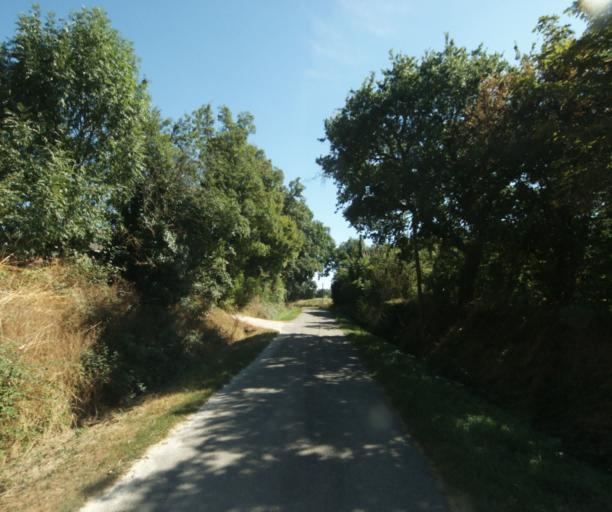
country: FR
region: Midi-Pyrenees
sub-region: Departement de la Haute-Garonne
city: Saint-Felix-Lauragais
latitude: 43.5082
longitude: 1.8914
